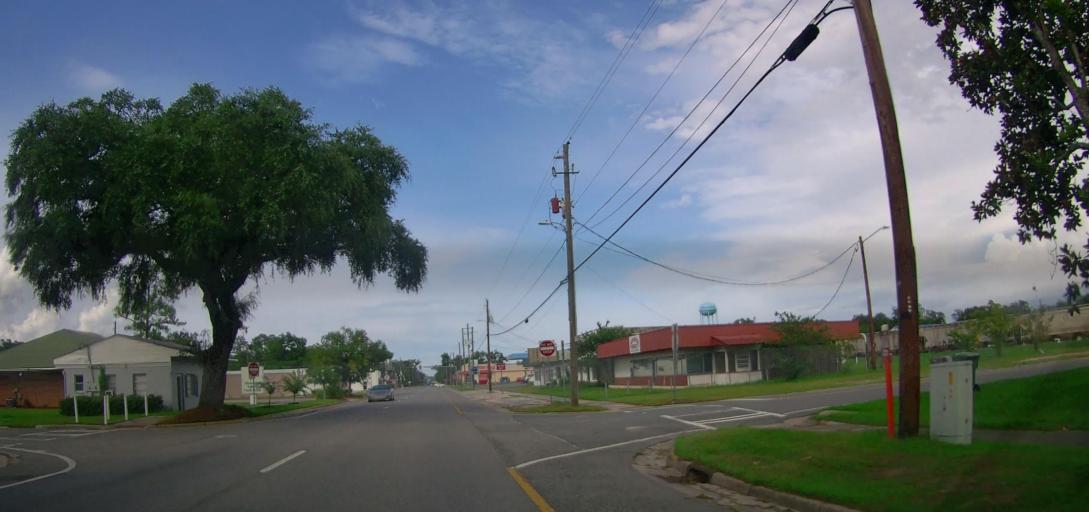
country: US
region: Georgia
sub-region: Wayne County
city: Jesup
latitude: 31.4848
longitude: -82.0188
